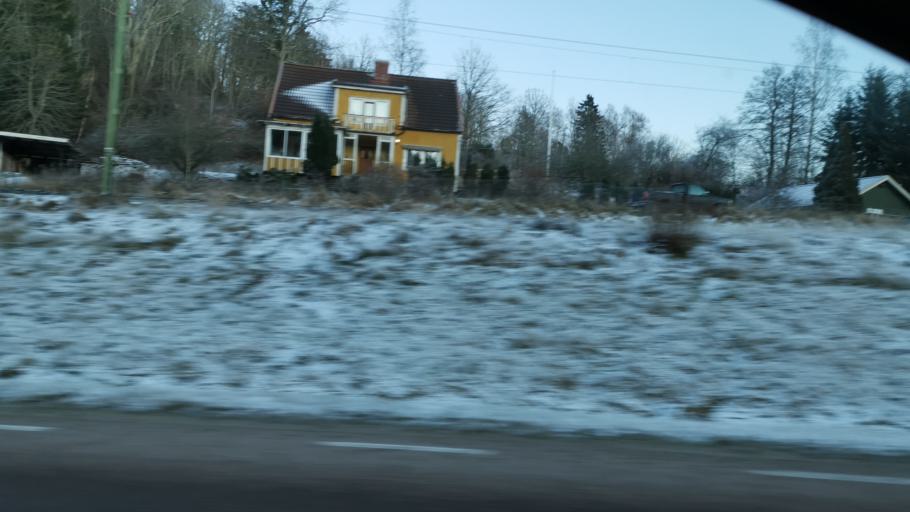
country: SE
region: Vaestra Goetaland
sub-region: Munkedals Kommun
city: Munkedal
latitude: 58.4146
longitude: 11.7329
